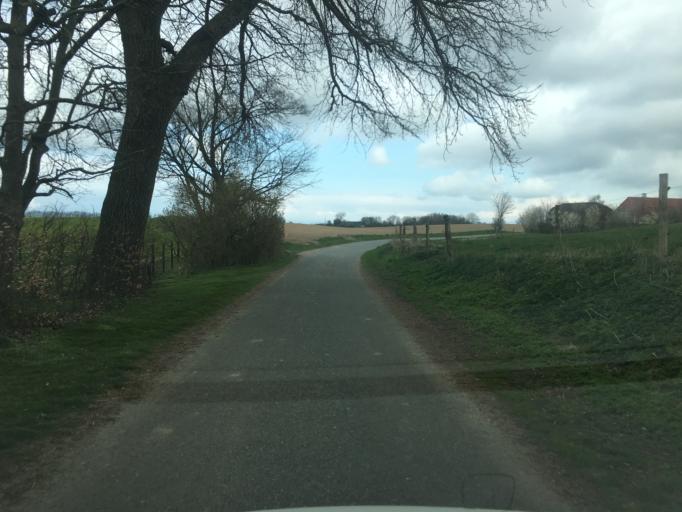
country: DK
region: South Denmark
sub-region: Sonderborg Kommune
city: Grasten
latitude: 54.9845
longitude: 9.5174
